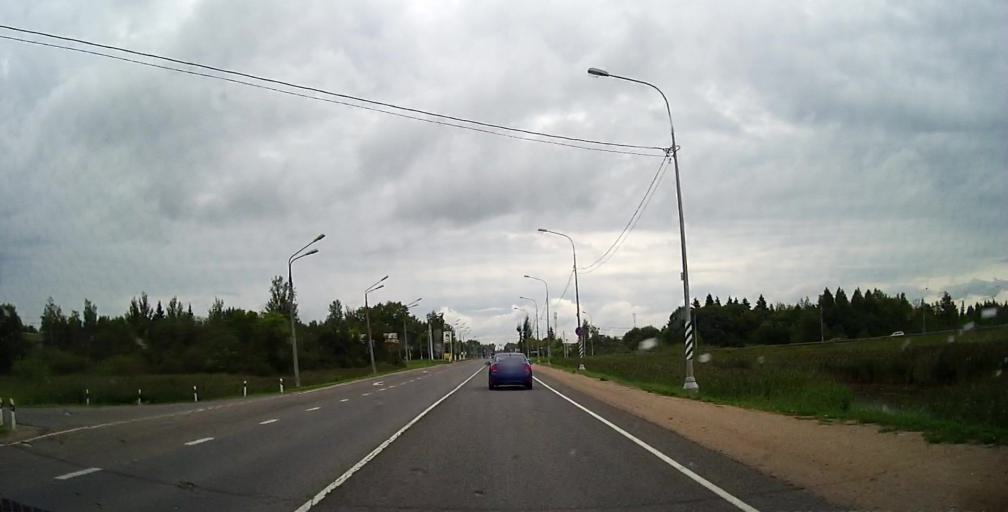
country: RU
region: Smolensk
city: Katyn'
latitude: 54.7786
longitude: 31.8017
